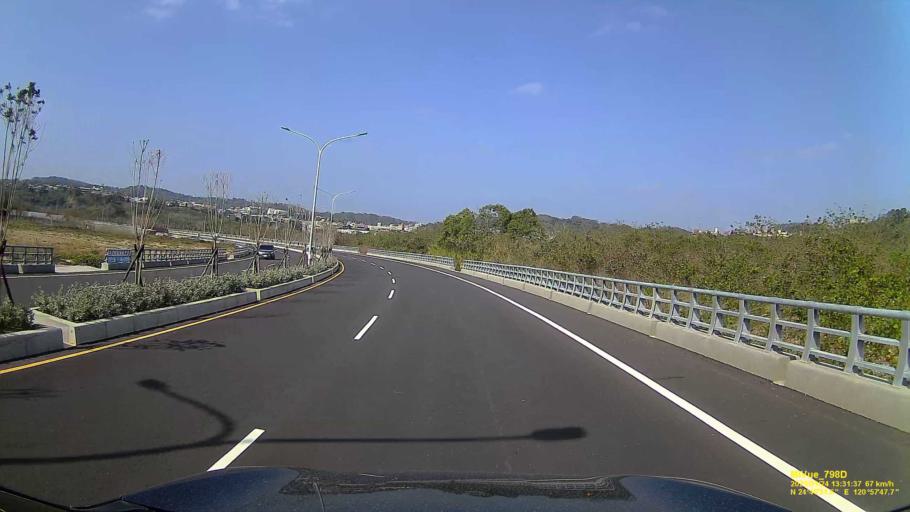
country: TW
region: Taiwan
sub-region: Hsinchu
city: Hsinchu
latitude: 24.6757
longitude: 120.9632
